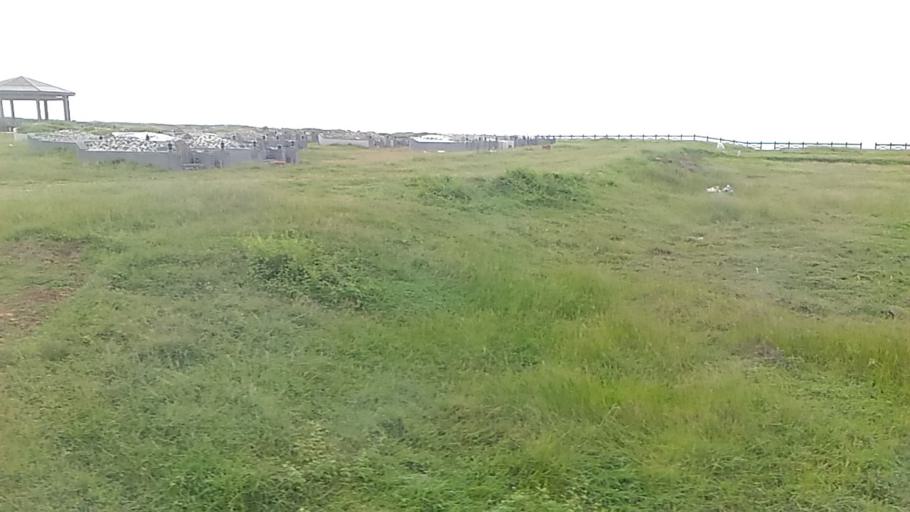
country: TW
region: Taiwan
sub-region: Penghu
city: Ma-kung
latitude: 23.2198
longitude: 119.4424
